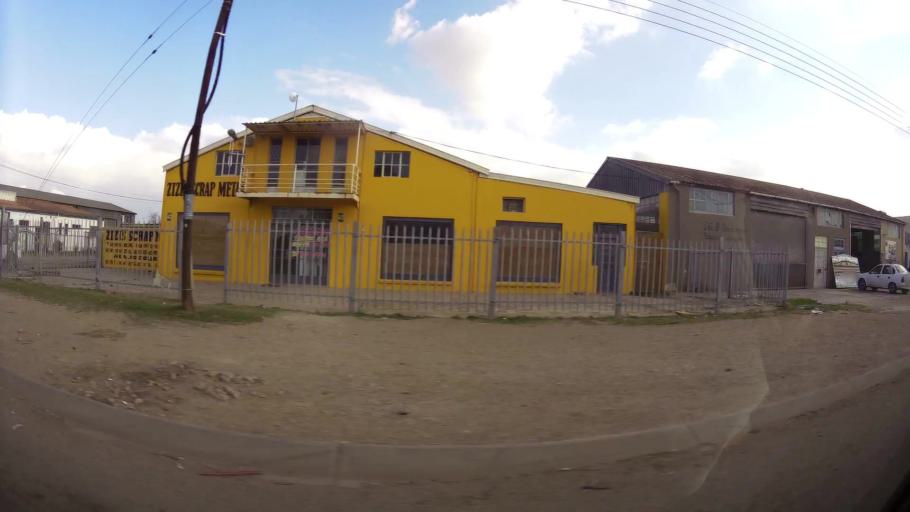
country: ZA
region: Eastern Cape
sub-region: Nelson Mandela Bay Metropolitan Municipality
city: Uitenhage
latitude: -33.7747
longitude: 25.3943
